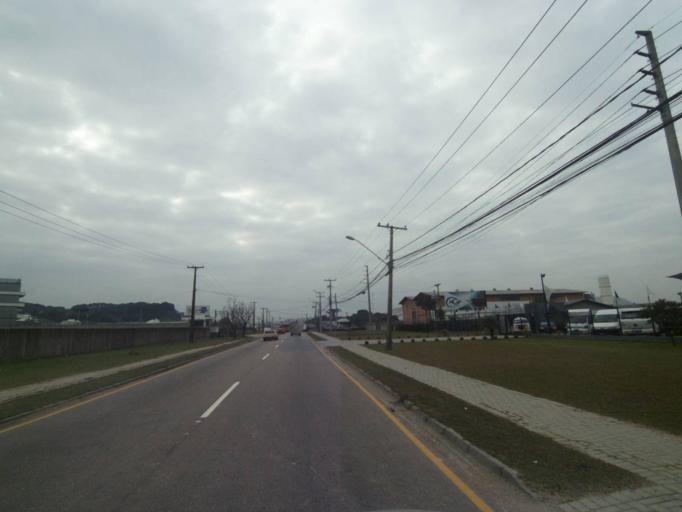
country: BR
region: Parana
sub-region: Curitiba
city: Curitiba
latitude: -25.5195
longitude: -49.3255
